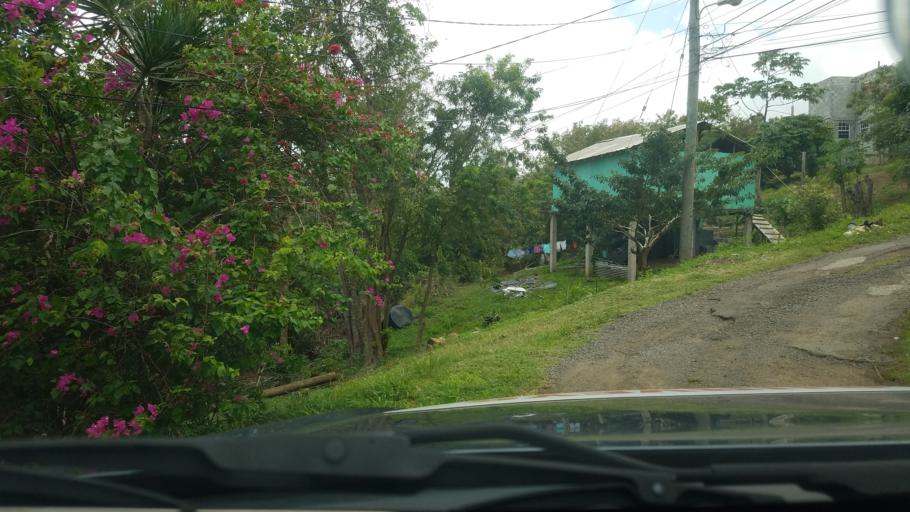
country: LC
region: Gros-Islet
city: Gros Islet
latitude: 14.0580
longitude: -60.9343
